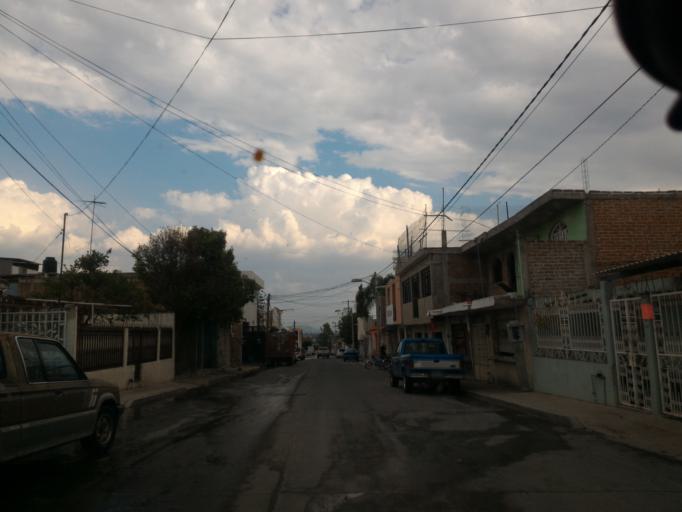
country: MX
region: Guanajuato
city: San Francisco del Rincon
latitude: 21.0420
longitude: -101.8565
